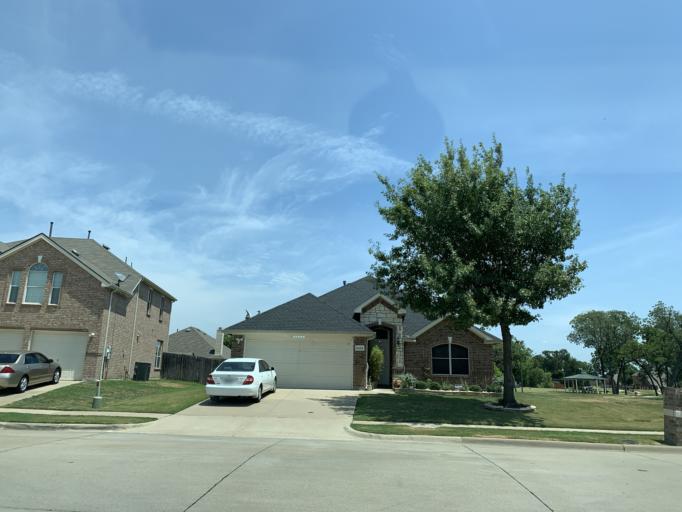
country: US
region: Texas
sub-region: Dallas County
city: Cedar Hill
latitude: 32.6439
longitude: -97.0218
